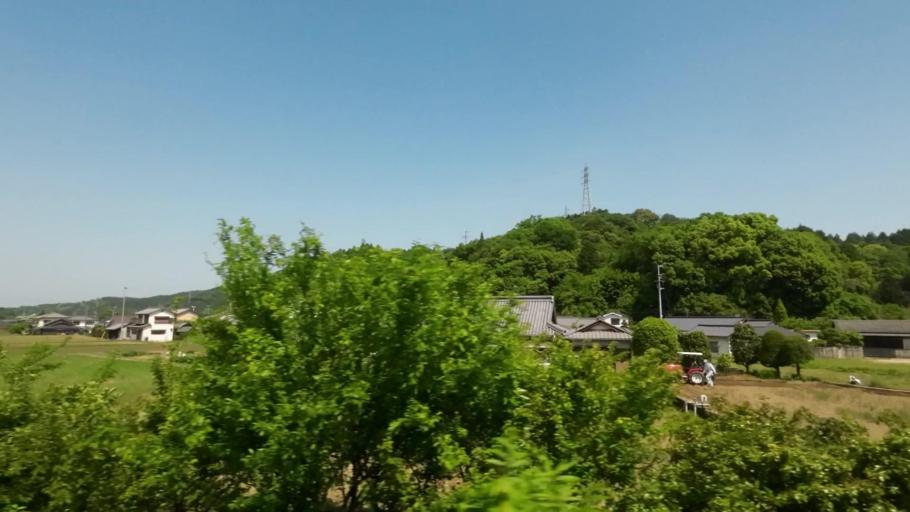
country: JP
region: Ehime
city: Niihama
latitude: 33.9253
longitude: 133.2504
